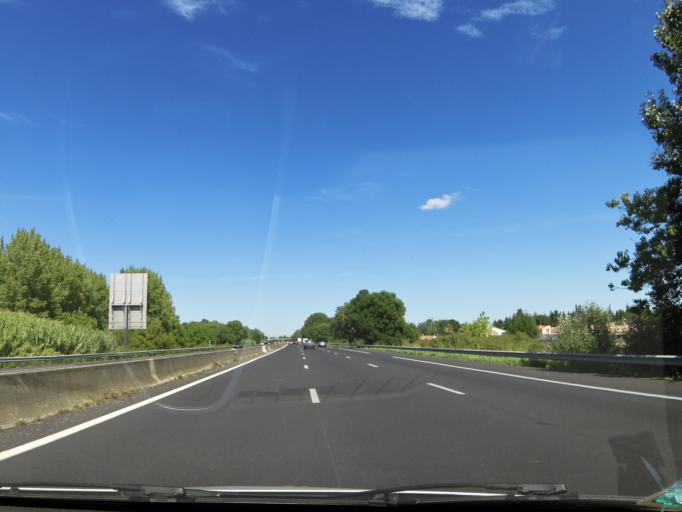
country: FR
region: Languedoc-Roussillon
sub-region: Departement du Gard
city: Caissargues
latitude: 43.8190
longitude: 4.3738
